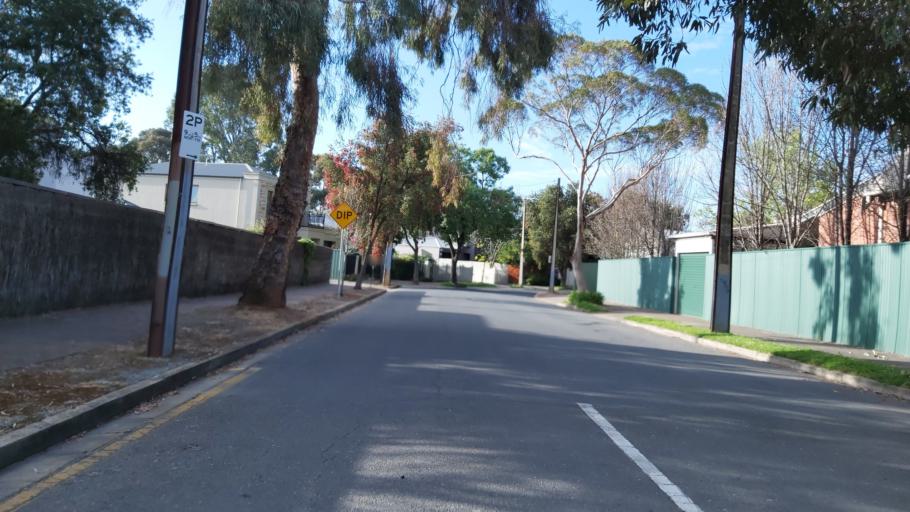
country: AU
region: South Australia
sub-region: Unley
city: Fullarton
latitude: -34.9506
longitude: 138.6288
